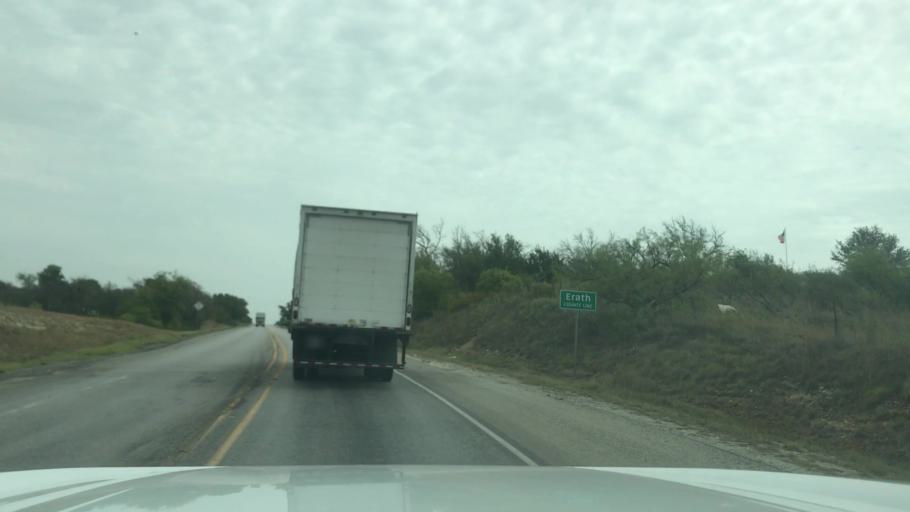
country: US
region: Texas
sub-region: Erath County
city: Dublin
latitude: 32.0877
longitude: -98.4296
